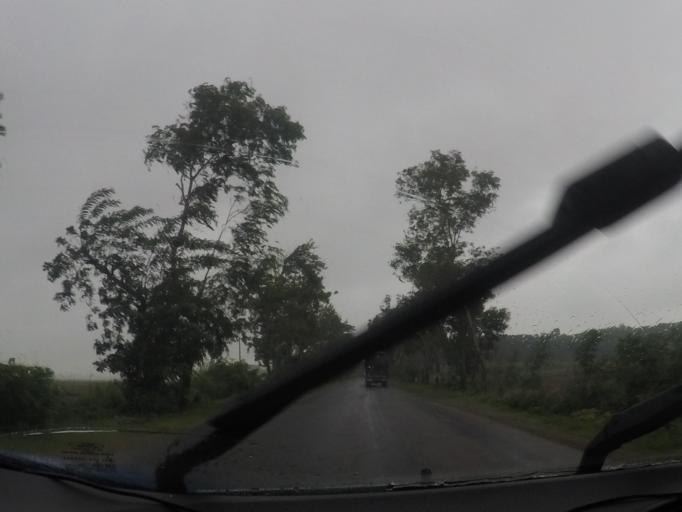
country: MM
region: Bago
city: Letpandan
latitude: 18.1586
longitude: 95.6863
